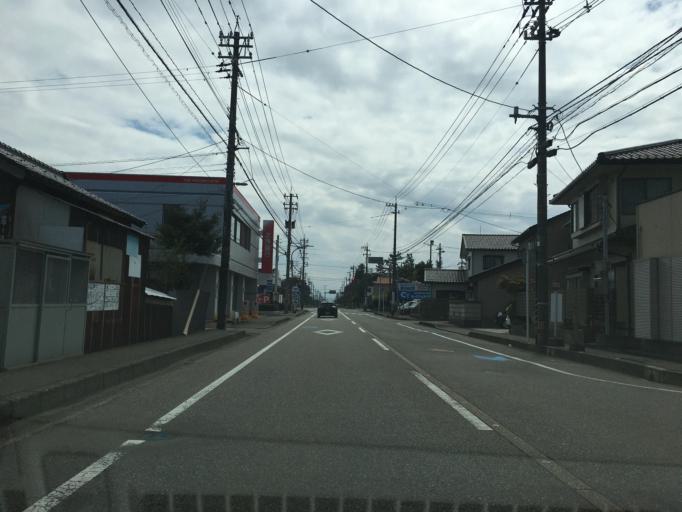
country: JP
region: Toyama
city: Kuragaki-kosugi
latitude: 36.7684
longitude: 137.1341
